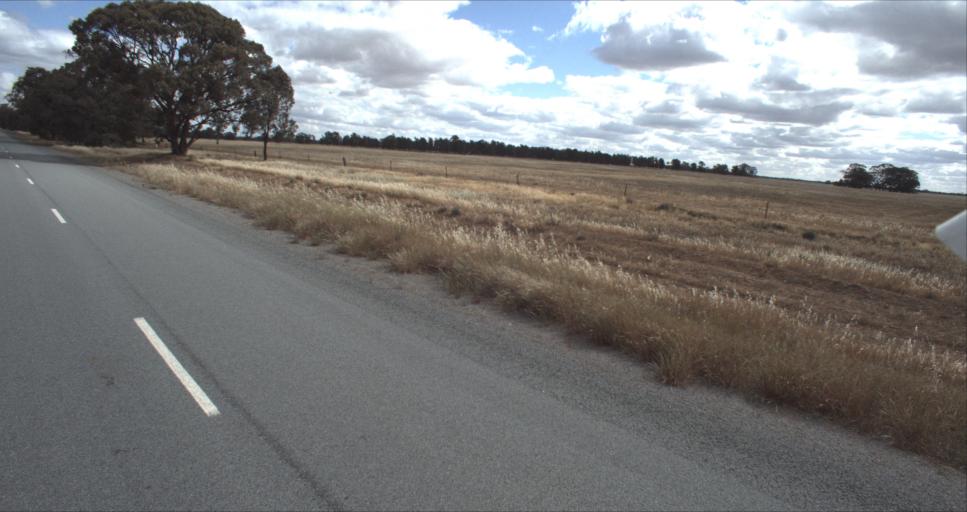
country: AU
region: New South Wales
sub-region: Leeton
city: Leeton
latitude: -34.6797
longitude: 146.3458
